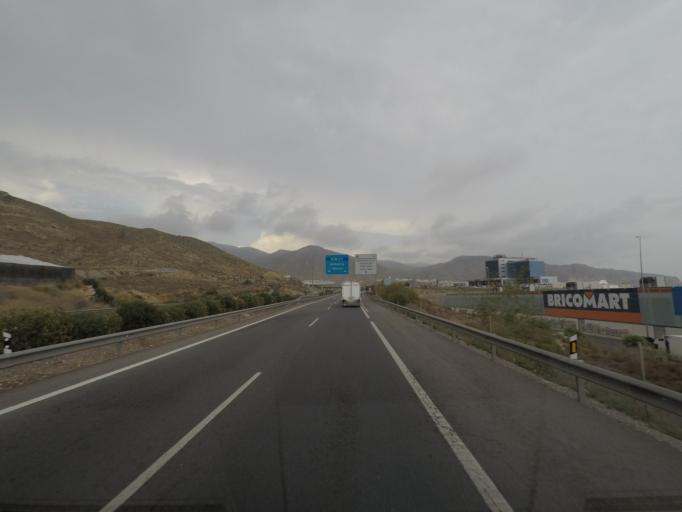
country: ES
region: Andalusia
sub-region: Provincia de Almeria
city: Aguadulce
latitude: 36.8175
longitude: -2.6018
